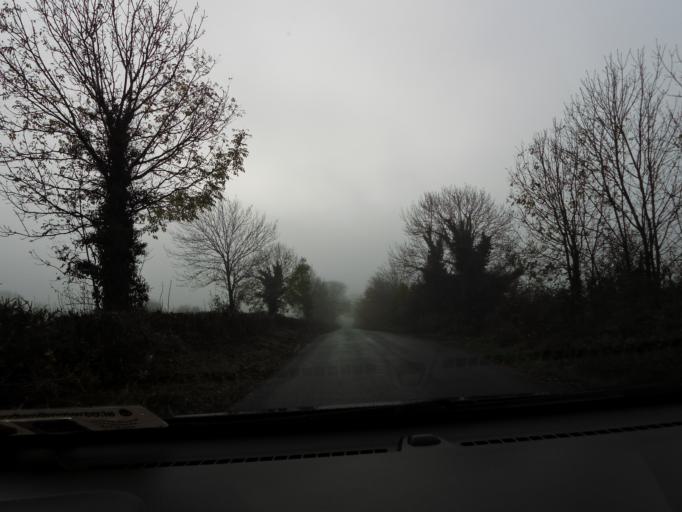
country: IE
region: Leinster
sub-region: An Iarmhi
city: Moate
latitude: 53.3840
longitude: -7.8040
